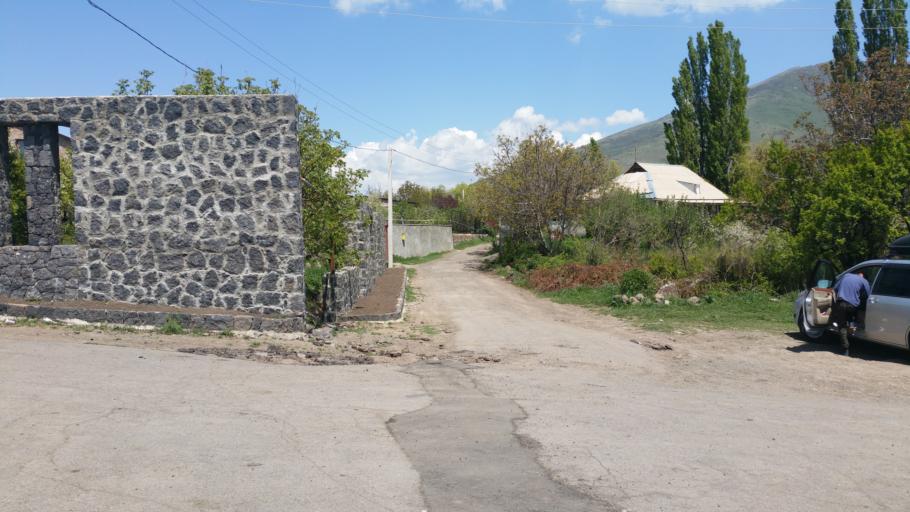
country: AM
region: Aragatsotn
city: Ushi
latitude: 40.3810
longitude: 44.3958
